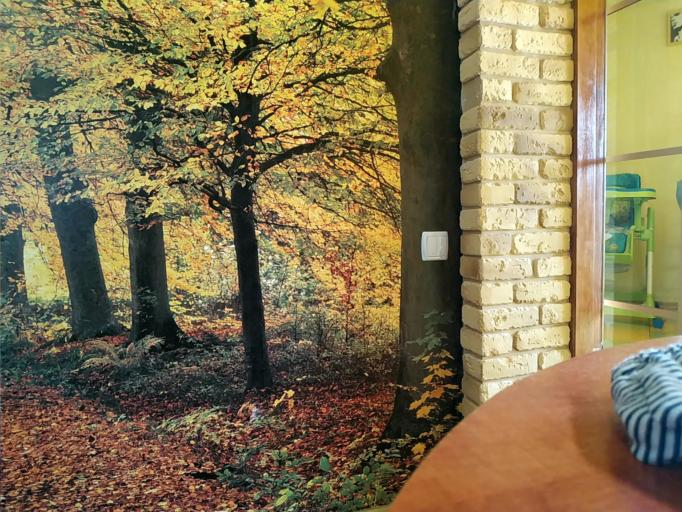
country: RU
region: Novgorod
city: Parfino
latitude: 57.7958
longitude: 31.6306
